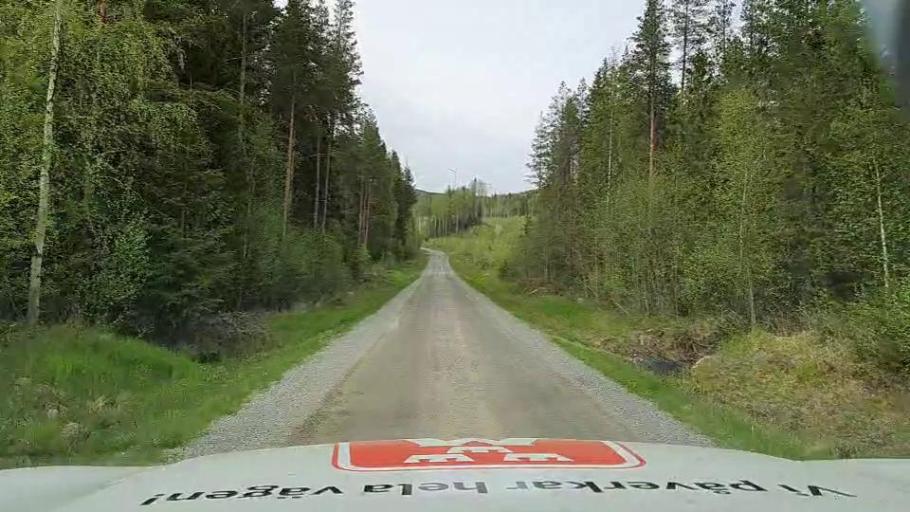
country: SE
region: Jaemtland
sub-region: Bergs Kommun
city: Hoverberg
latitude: 62.5257
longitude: 14.9146
